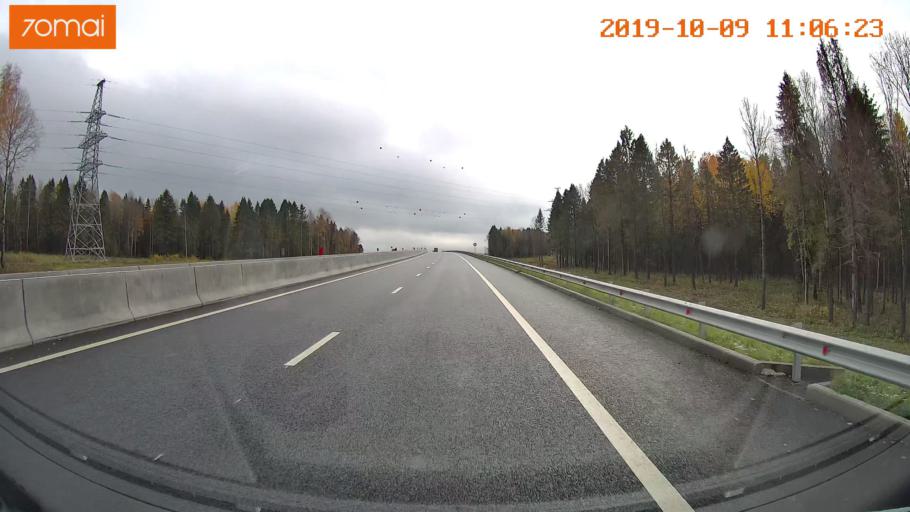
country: RU
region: Vologda
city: Vologda
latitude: 59.1872
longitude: 39.7602
